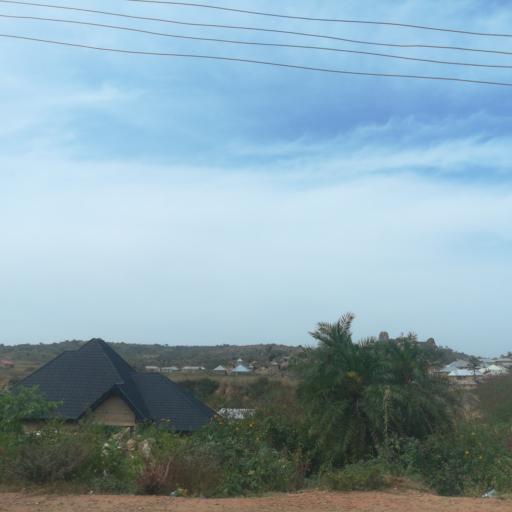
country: NG
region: Plateau
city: Jos
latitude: 9.8843
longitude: 8.8651
